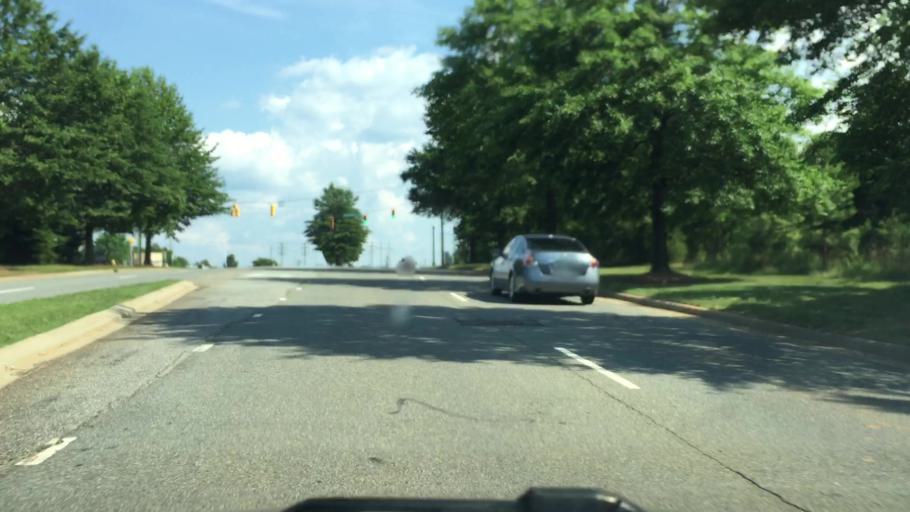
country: US
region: North Carolina
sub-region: Iredell County
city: Mooresville
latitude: 35.5831
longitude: -80.8819
